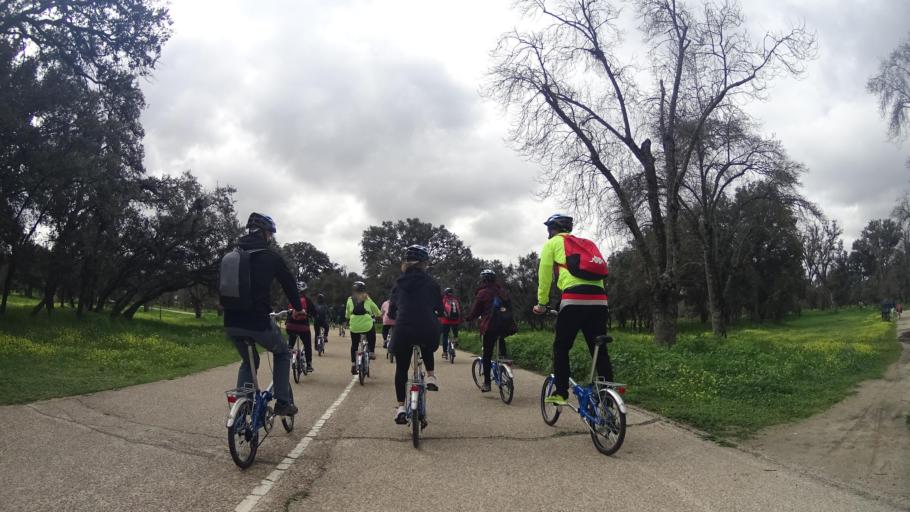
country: ES
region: Madrid
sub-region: Provincia de Madrid
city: Latina
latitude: 40.4137
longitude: -3.7561
